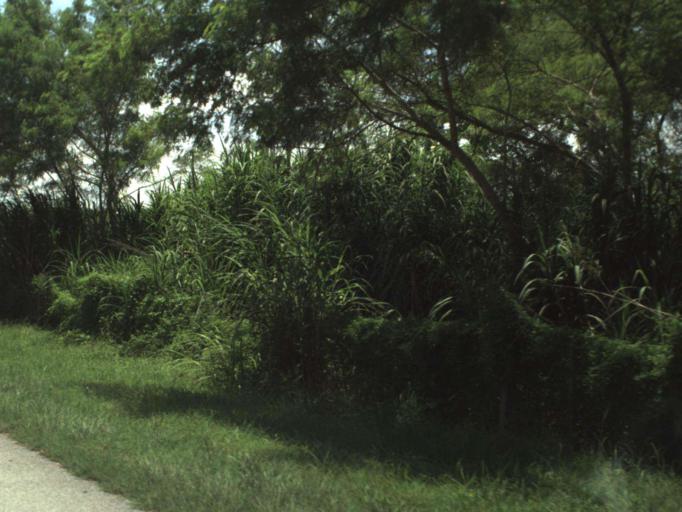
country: US
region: Florida
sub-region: Palm Beach County
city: Pahokee
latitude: 26.9360
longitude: -80.6108
